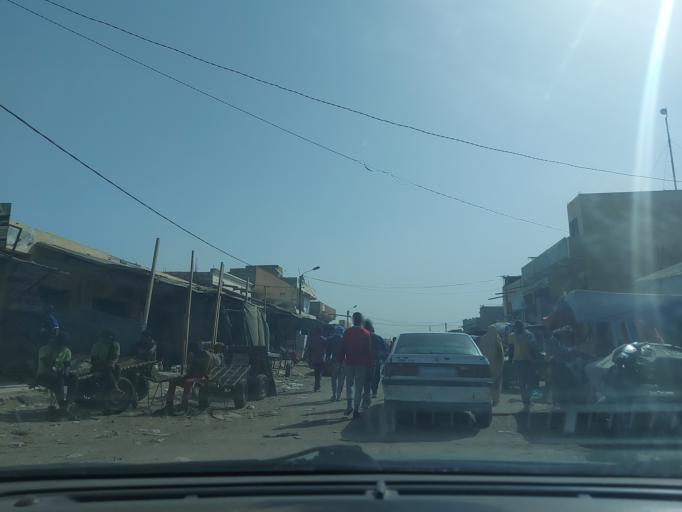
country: MR
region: Nouakchott
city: Nouakchott
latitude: 18.0728
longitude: -15.9920
